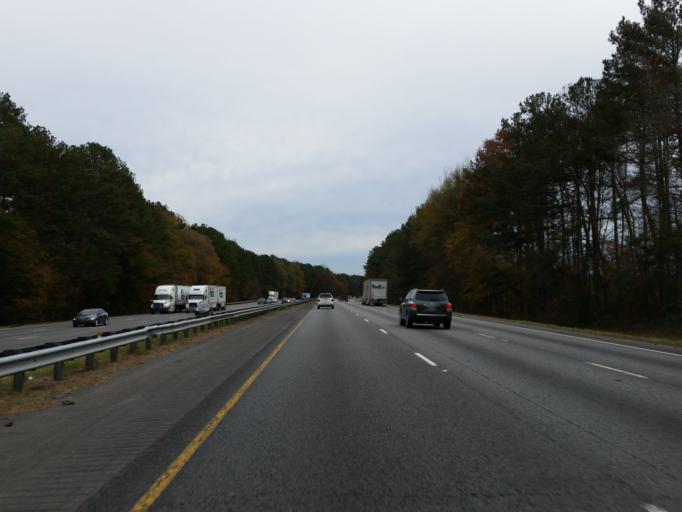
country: US
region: Georgia
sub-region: Monroe County
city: Forsyth
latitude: 33.1285
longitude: -84.0102
